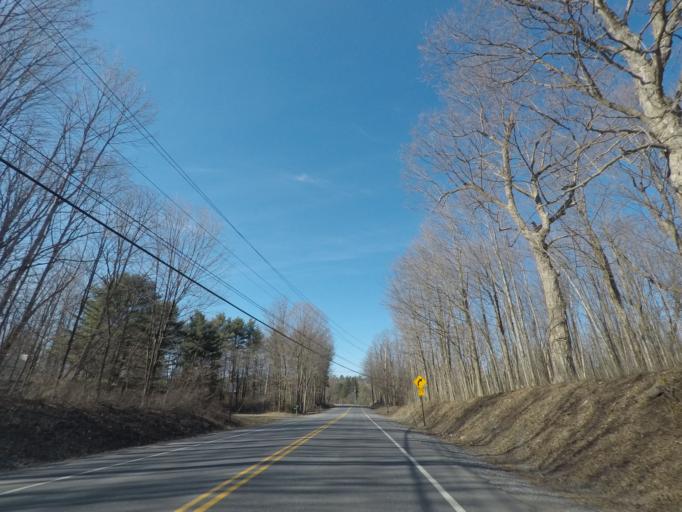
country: US
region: New York
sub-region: Saratoga County
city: Milton
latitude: 43.0720
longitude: -73.8480
